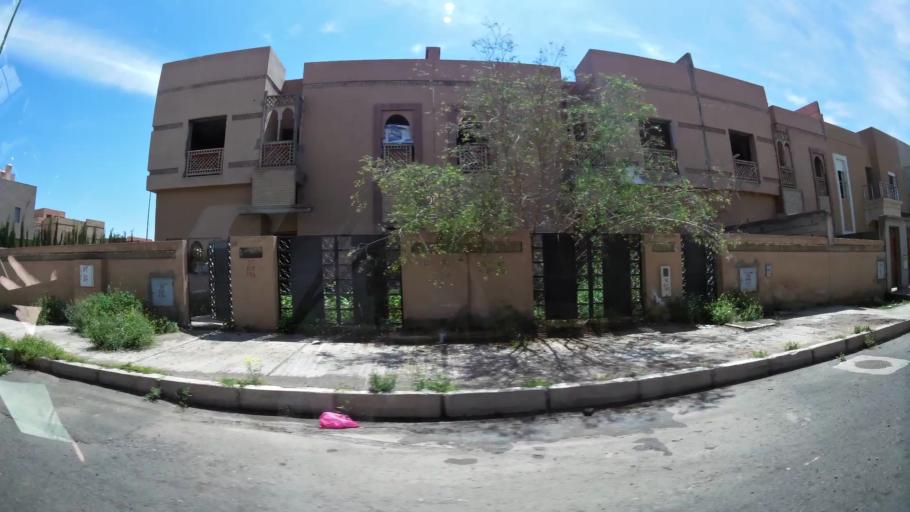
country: MA
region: Marrakech-Tensift-Al Haouz
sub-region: Marrakech
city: Marrakesh
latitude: 31.6512
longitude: -8.0723
